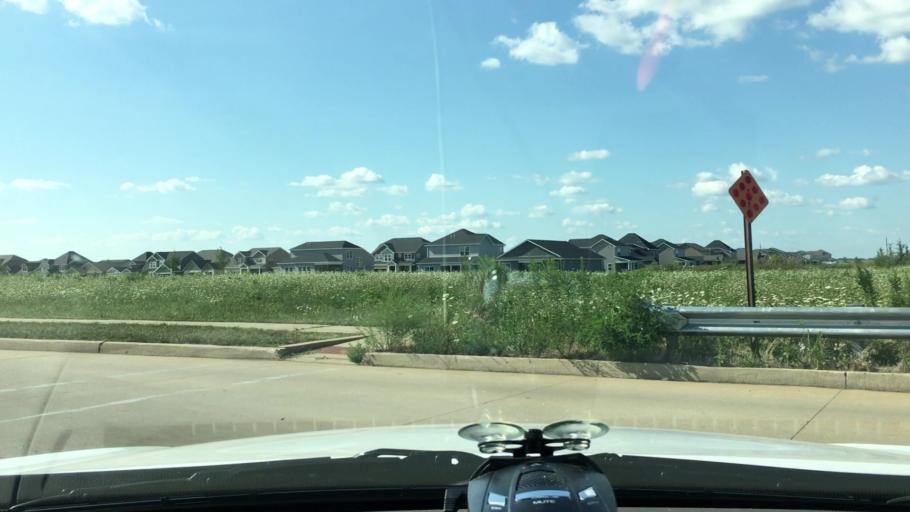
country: US
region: Illinois
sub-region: Champaign County
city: Champaign
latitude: 40.1491
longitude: -88.2486
